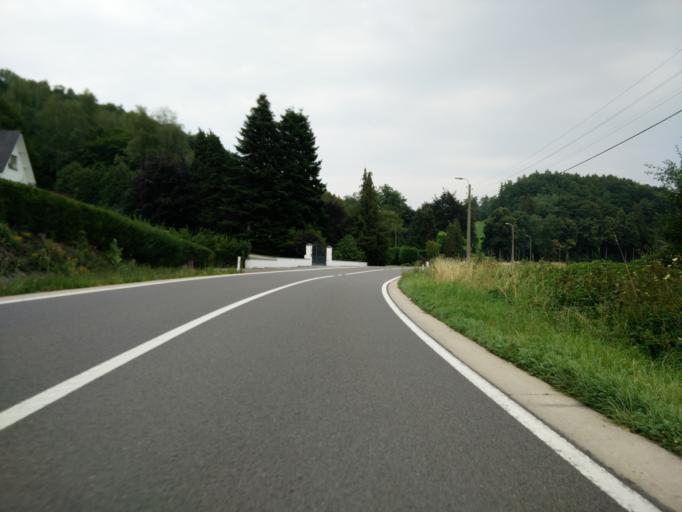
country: BE
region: Flanders
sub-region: Provincie Limburg
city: Sint-Pieters-Voeren
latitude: 50.7041
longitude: 5.7970
